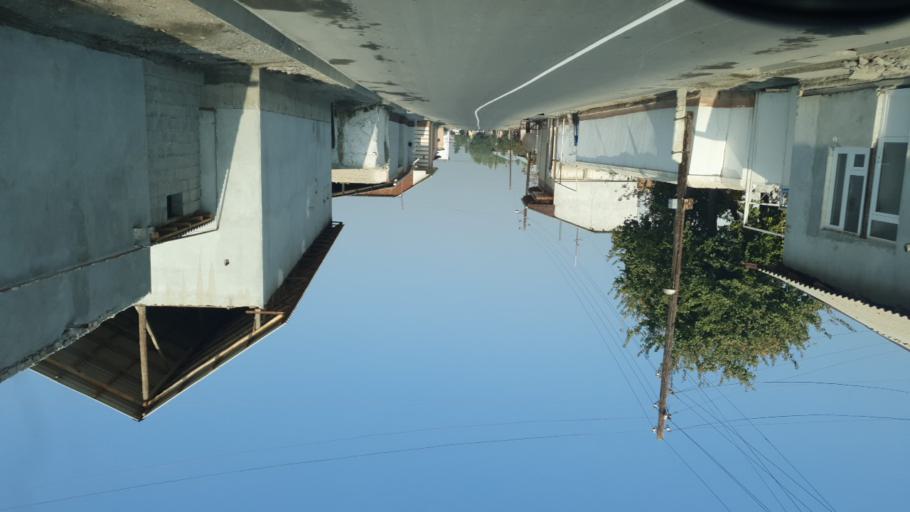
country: UZ
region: Fergana
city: Qo`qon
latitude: 40.5854
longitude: 70.9070
